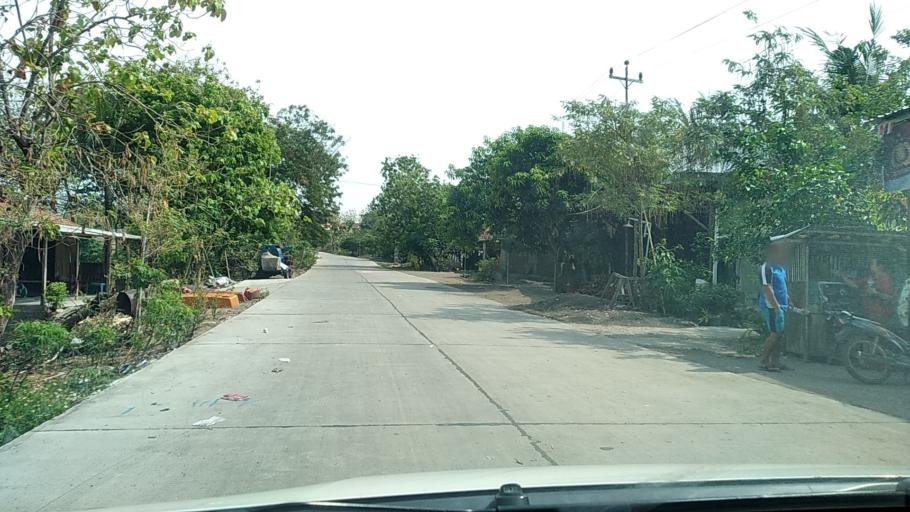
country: ID
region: Central Java
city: Mranggen
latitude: -7.0683
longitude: 110.4823
